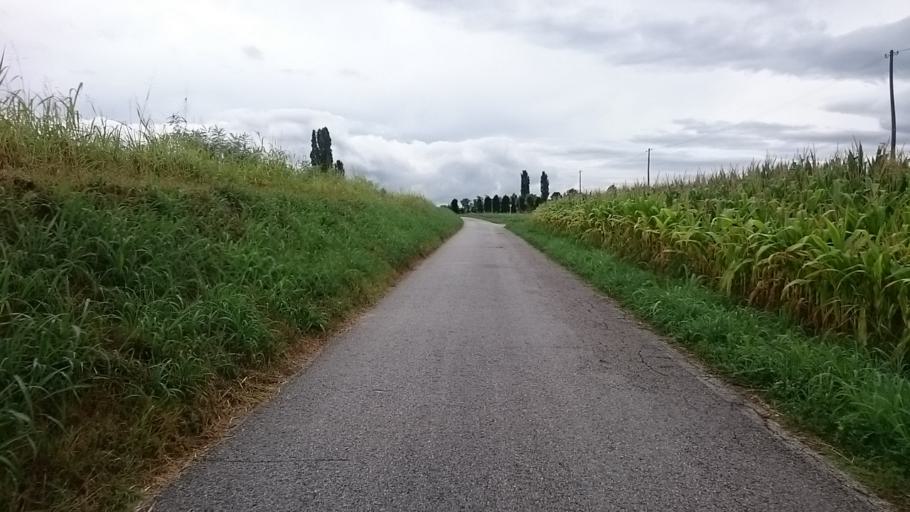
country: IT
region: Veneto
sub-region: Provincia di Padova
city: Loreggiola
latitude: 45.6363
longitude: 11.9243
